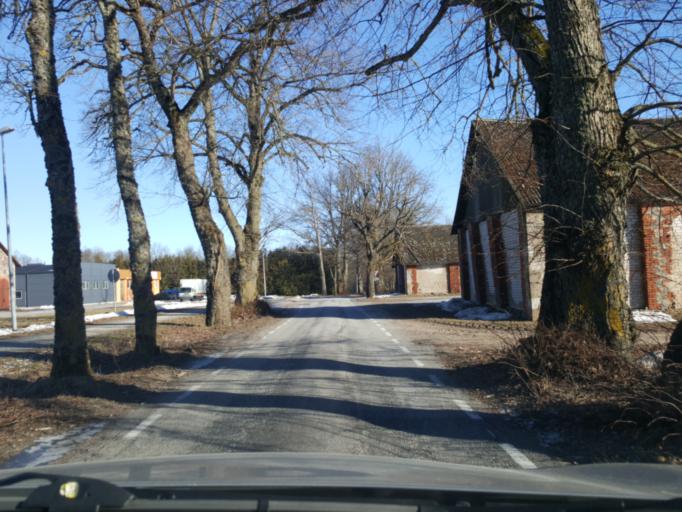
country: EE
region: Viljandimaa
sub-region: Vohma linn
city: Vohma
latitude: 58.5516
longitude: 25.5585
